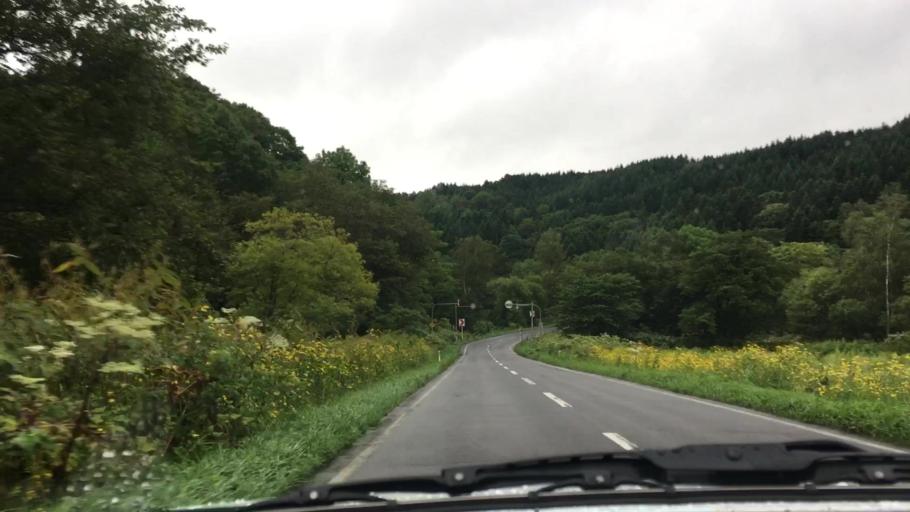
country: JP
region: Hokkaido
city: Niseko Town
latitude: 42.6598
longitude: 140.7579
